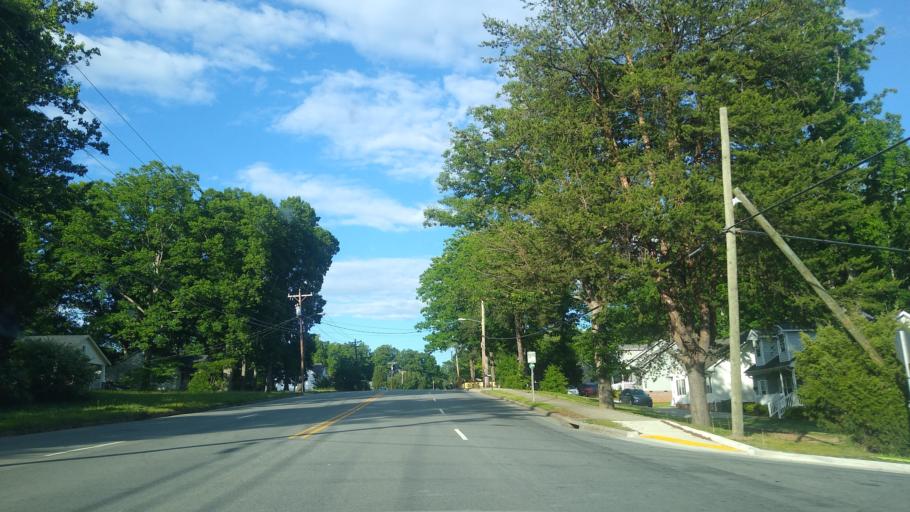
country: US
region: North Carolina
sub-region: Guilford County
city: Greensboro
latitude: 36.1435
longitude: -79.7685
